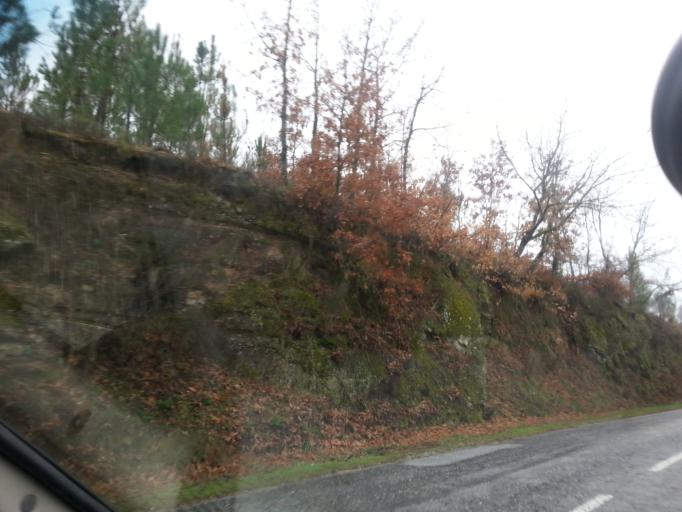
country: PT
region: Guarda
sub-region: Fornos de Algodres
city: Fornos de Algodres
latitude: 40.6246
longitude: -7.4734
